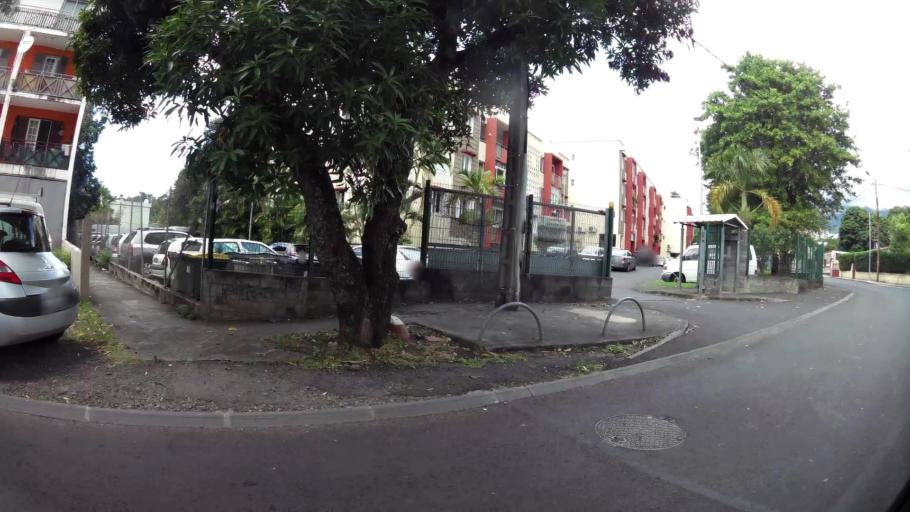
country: RE
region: Reunion
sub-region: Reunion
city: Saint-Denis
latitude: -20.8897
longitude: 55.4742
